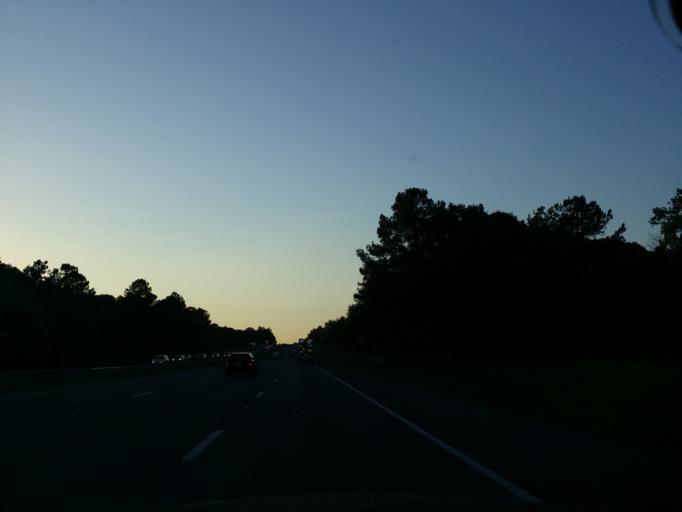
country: US
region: Florida
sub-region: Columbia County
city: Five Points
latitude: 30.2249
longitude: -82.7174
